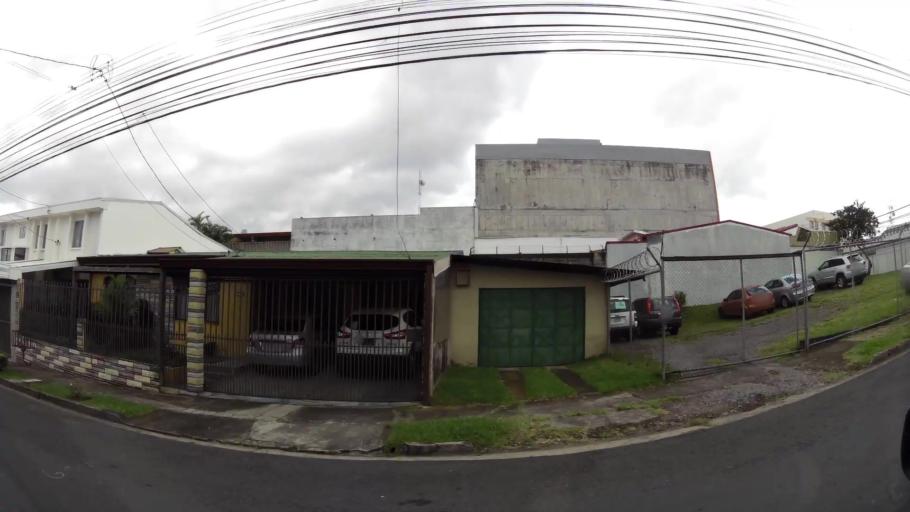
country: CR
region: San Jose
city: San Pedro
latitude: 9.9283
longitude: -84.0535
